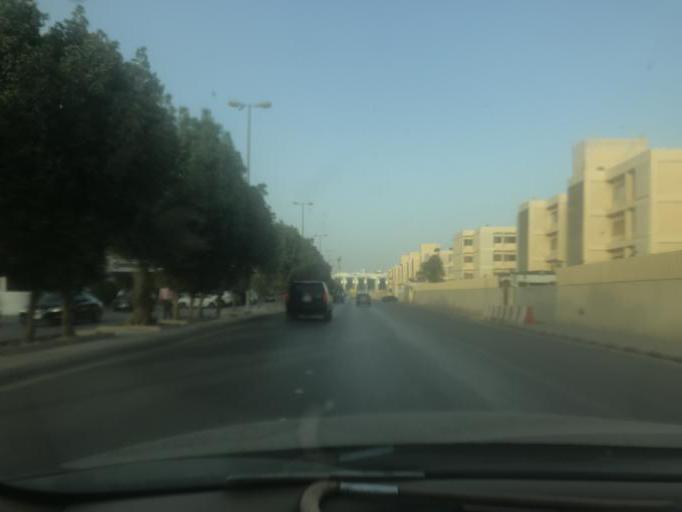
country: SA
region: Ar Riyad
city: Riyadh
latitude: 24.7097
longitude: 46.6817
